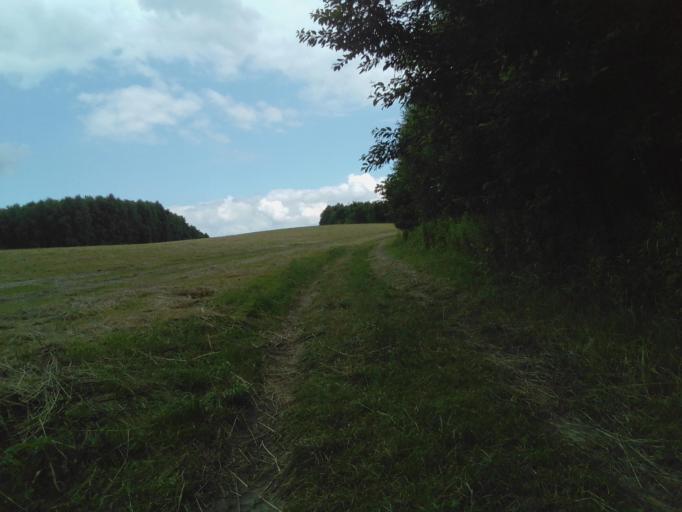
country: PL
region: Subcarpathian Voivodeship
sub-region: Powiat strzyzowski
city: Strzyzow
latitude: 49.8810
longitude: 21.7826
